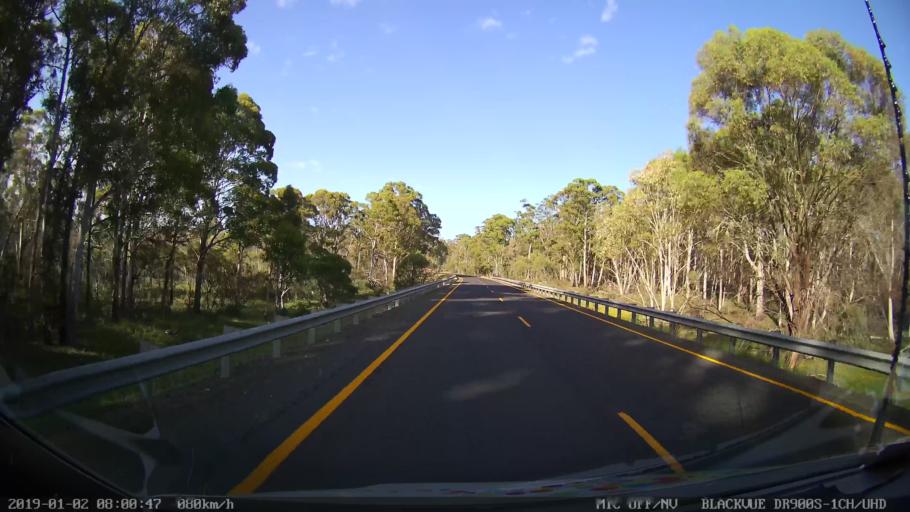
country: AU
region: New South Wales
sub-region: Tumut Shire
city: Tumut
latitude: -35.6458
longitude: 148.4405
